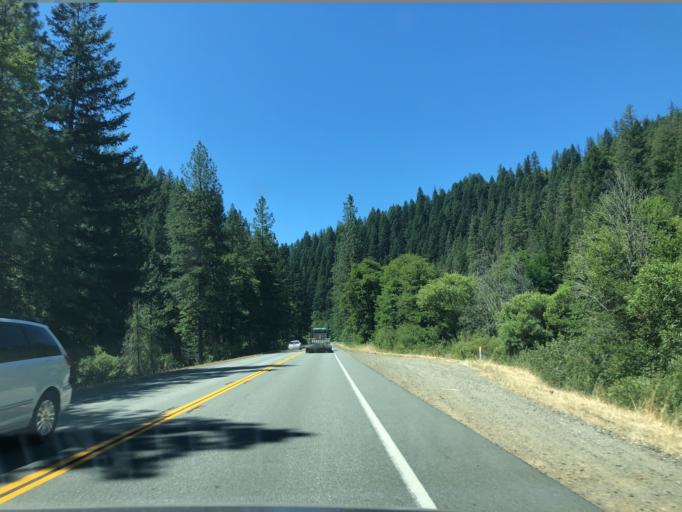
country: US
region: California
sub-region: Trinity County
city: Weaverville
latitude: 40.6930
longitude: -122.9309
